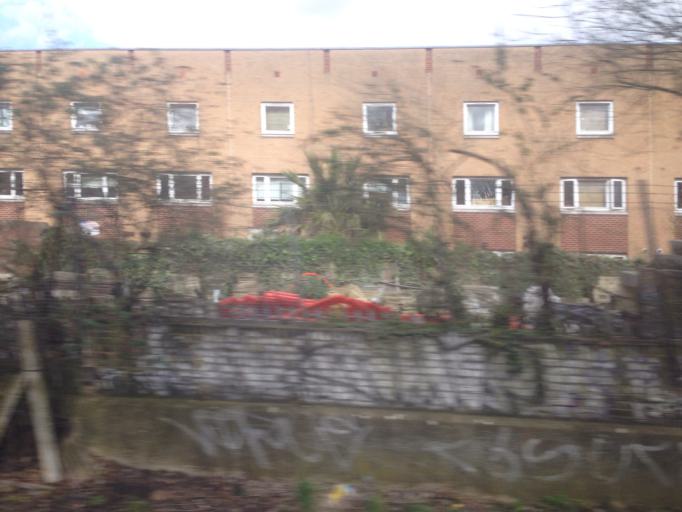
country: GB
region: England
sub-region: Greater London
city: Chelsea
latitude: 51.4790
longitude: -0.1859
